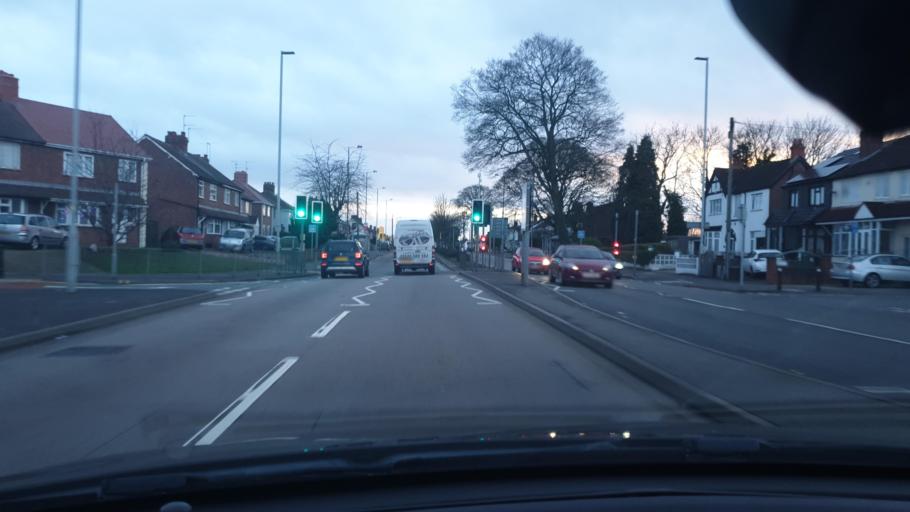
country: GB
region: England
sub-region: Staffordshire
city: Featherstone
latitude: 52.6277
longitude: -2.1267
